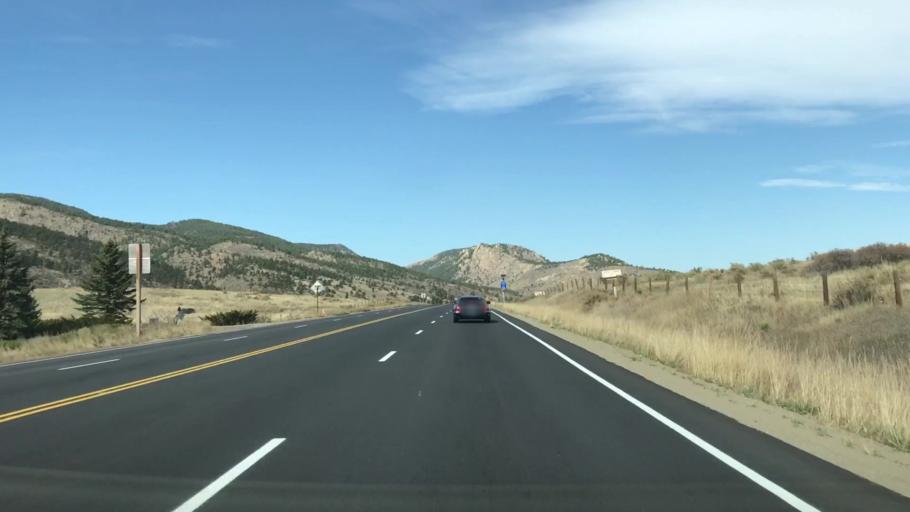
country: US
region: Colorado
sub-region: Larimer County
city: Loveland
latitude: 40.4143
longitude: -105.2175
